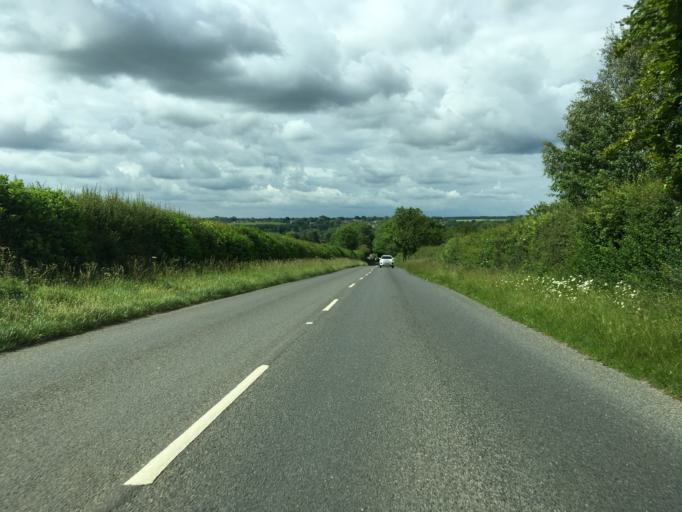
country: GB
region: England
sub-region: Oxfordshire
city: Burford
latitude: 51.8201
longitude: -1.6189
